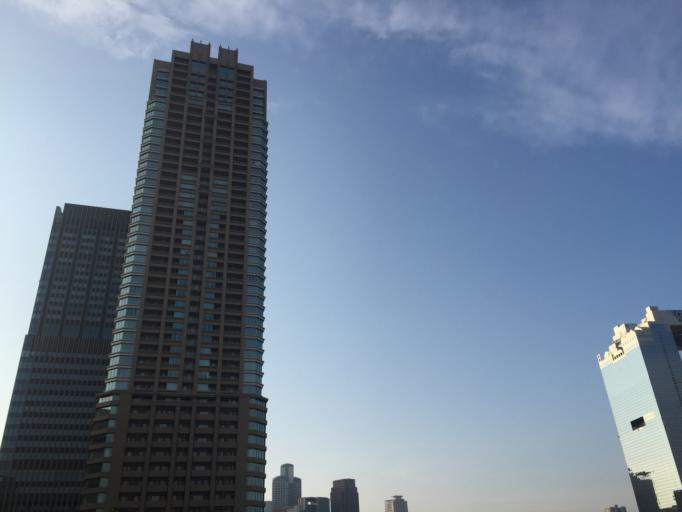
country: JP
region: Osaka
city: Osaka-shi
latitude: 34.7088
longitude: 135.4939
